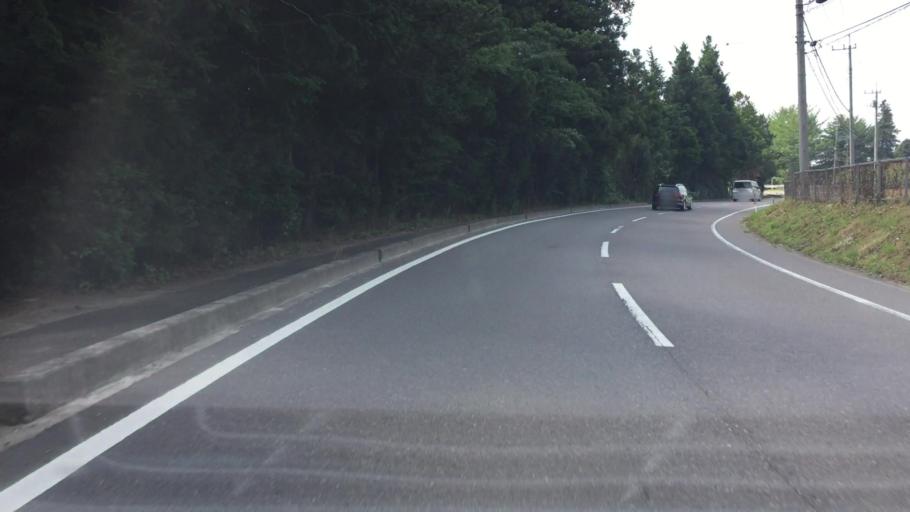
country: JP
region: Tochigi
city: Kuroiso
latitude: 37.0050
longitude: 139.9998
